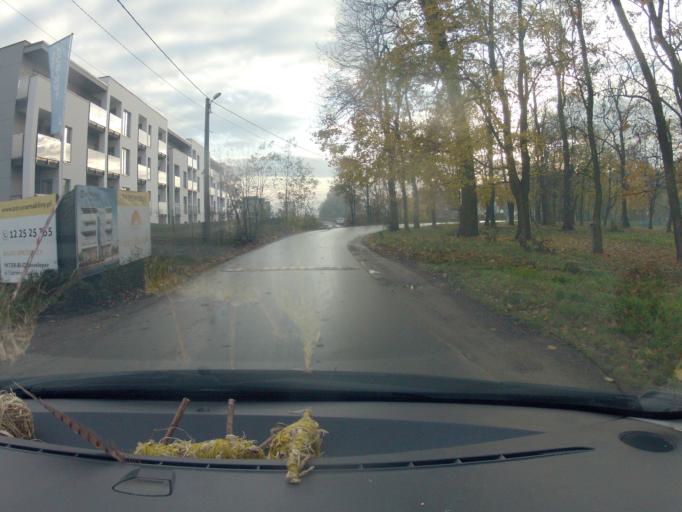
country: PL
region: Lesser Poland Voivodeship
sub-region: Krakow
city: Sidzina
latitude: 50.0027
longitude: 19.8889
